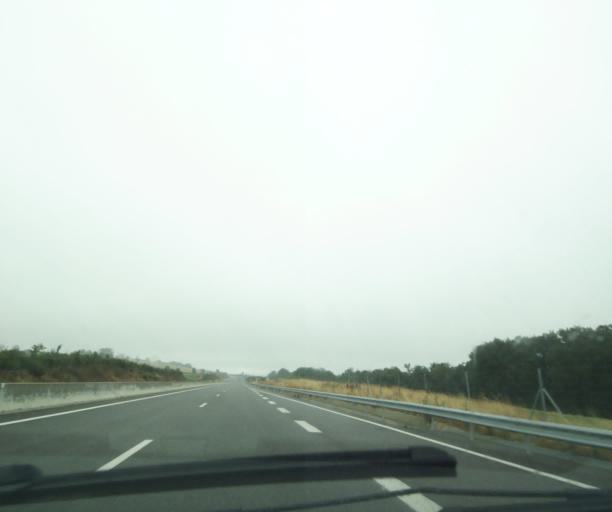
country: FR
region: Midi-Pyrenees
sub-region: Departement du Tarn
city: Carmaux
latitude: 44.0799
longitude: 2.2438
